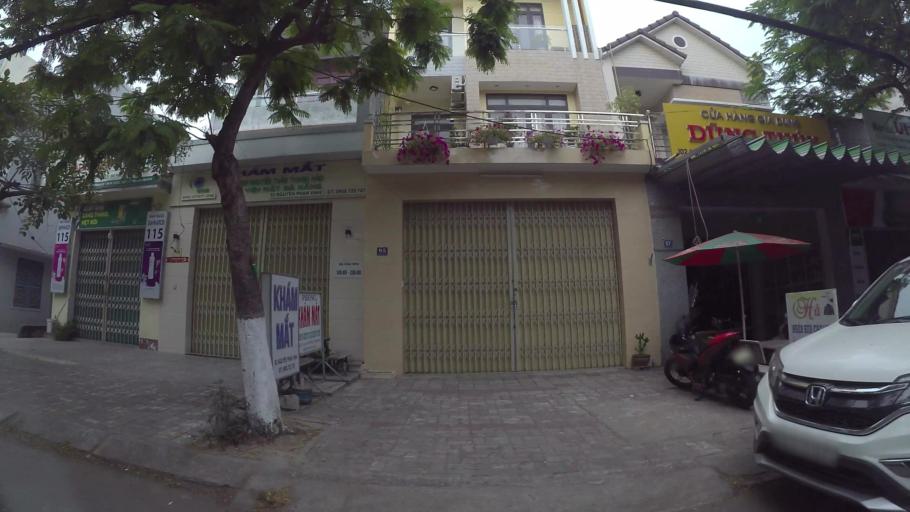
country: VN
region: Da Nang
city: Son Tra
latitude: 16.1005
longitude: 108.2521
